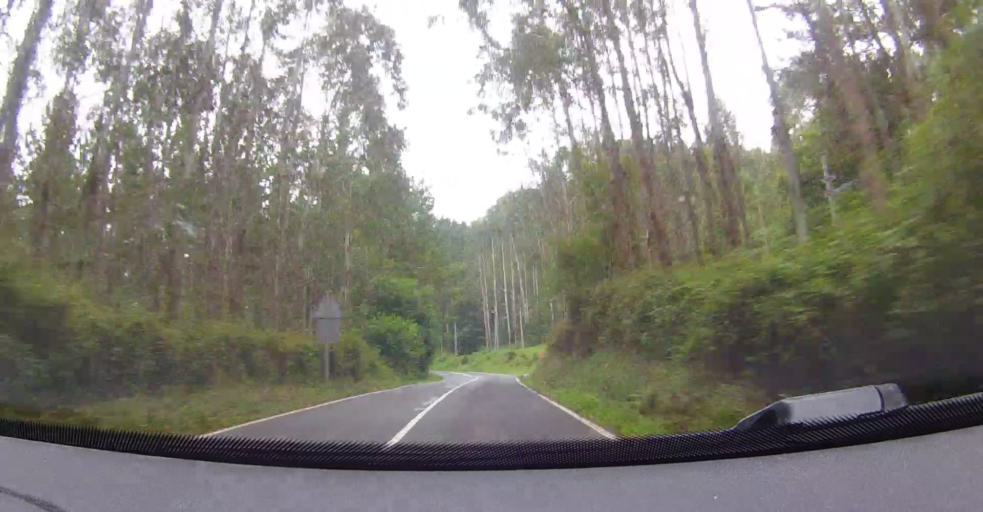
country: ES
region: Basque Country
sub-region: Bizkaia
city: Balmaseda
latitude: 43.2402
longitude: -3.2421
